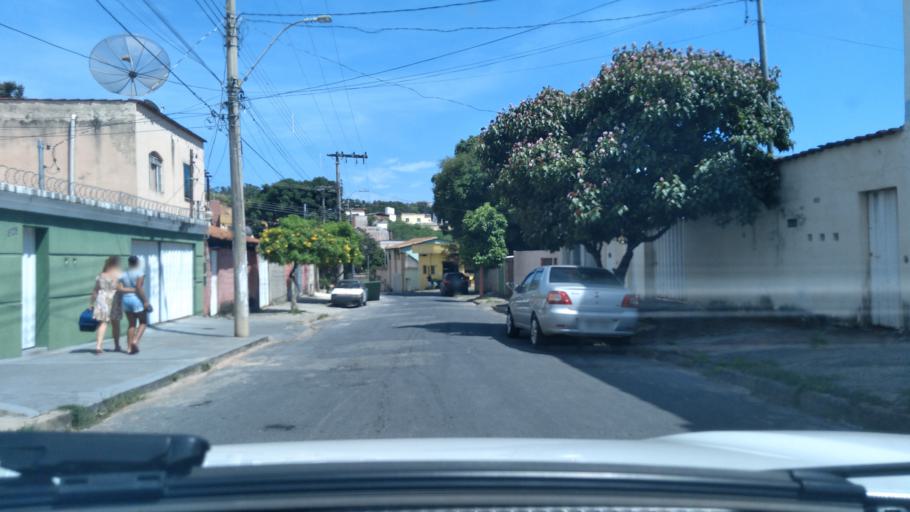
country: BR
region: Minas Gerais
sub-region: Contagem
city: Contagem
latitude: -19.9179
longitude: -44.0044
